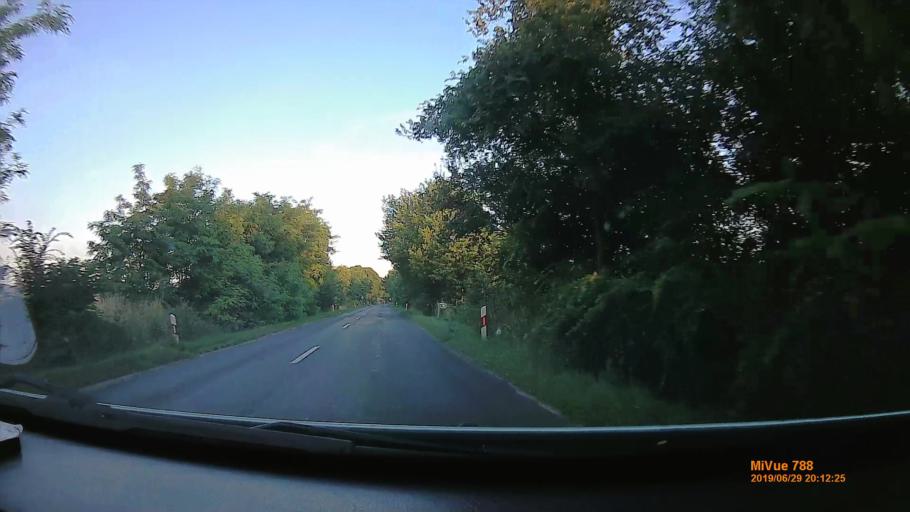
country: HU
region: Pest
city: Paty
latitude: 47.5182
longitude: 18.8045
